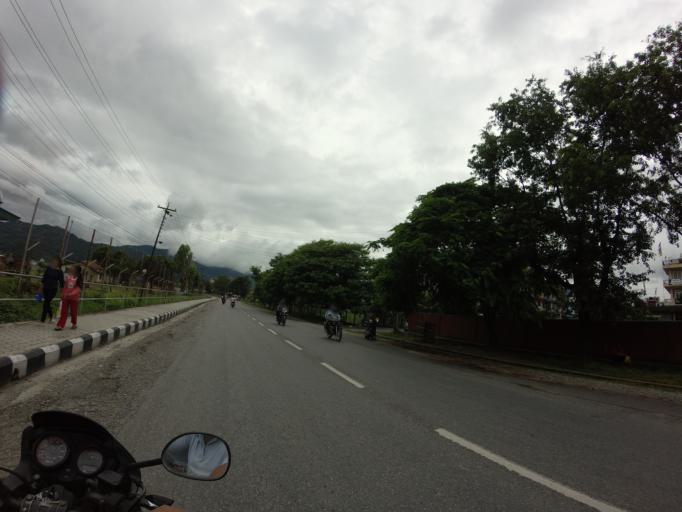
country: NP
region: Western Region
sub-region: Gandaki Zone
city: Pokhara
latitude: 28.1997
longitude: 83.9779
